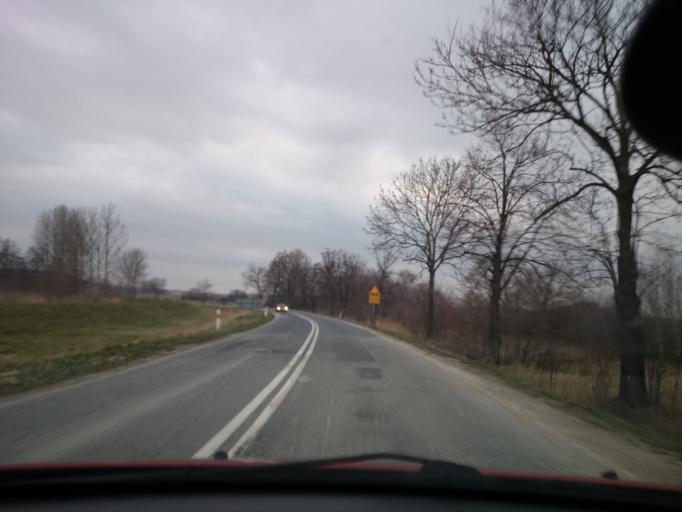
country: PL
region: Lower Silesian Voivodeship
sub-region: Powiat zabkowicki
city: Kamieniec Zabkowicki
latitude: 50.5090
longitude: 16.9322
